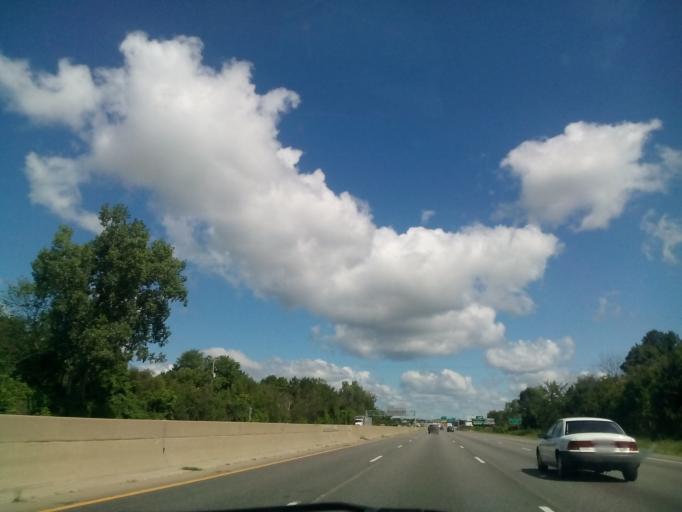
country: US
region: Michigan
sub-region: Genesee County
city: Flint
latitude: 42.9641
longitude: -83.7254
